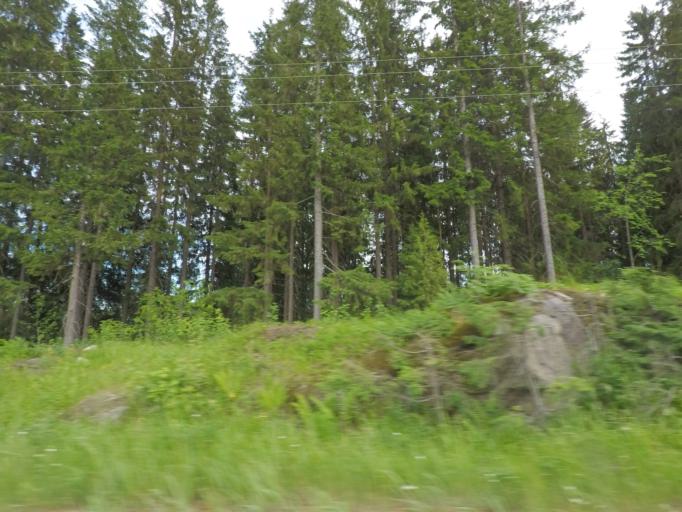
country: FI
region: Paijanne Tavastia
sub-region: Lahti
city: Lahti
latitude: 60.9282
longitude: 25.5820
